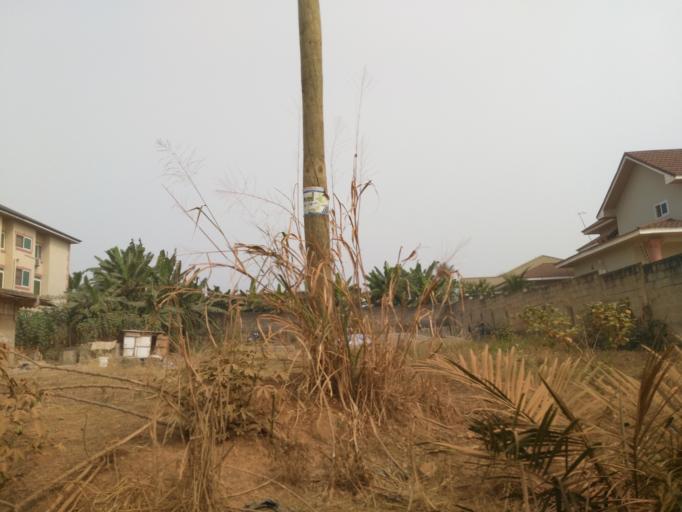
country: GH
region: Ashanti
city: Kumasi
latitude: 6.6410
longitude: -1.6306
